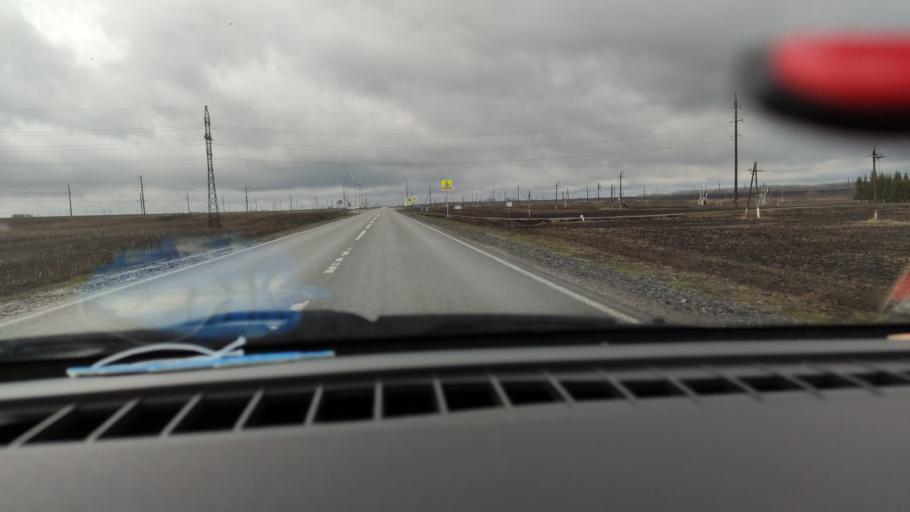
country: RU
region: Tatarstan
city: Nurlat
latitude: 54.4765
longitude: 50.8427
